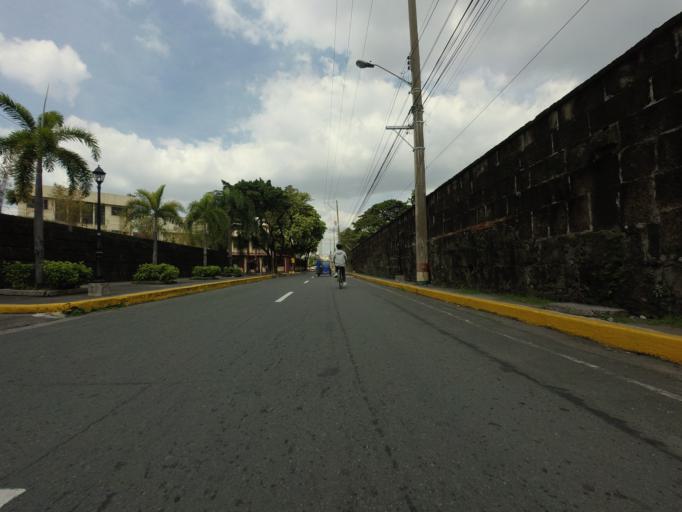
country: PH
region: Metro Manila
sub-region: City of Manila
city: Quiapo
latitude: 14.5883
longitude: 120.9787
